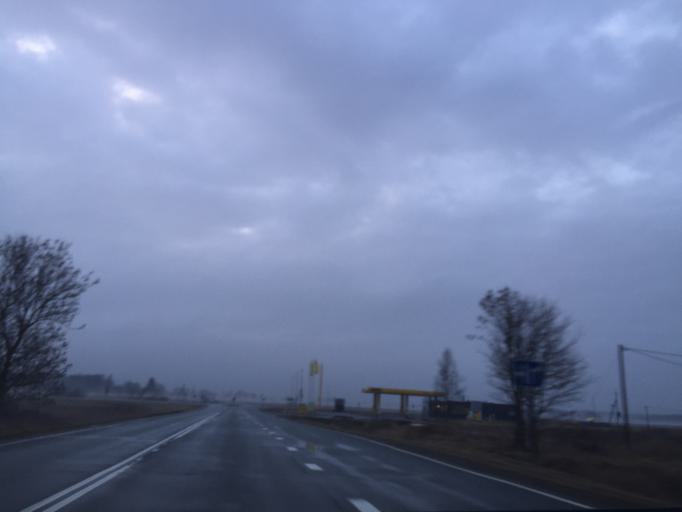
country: EE
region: Laeaene
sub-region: Lihula vald
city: Lihula
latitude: 58.6835
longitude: 23.8108
